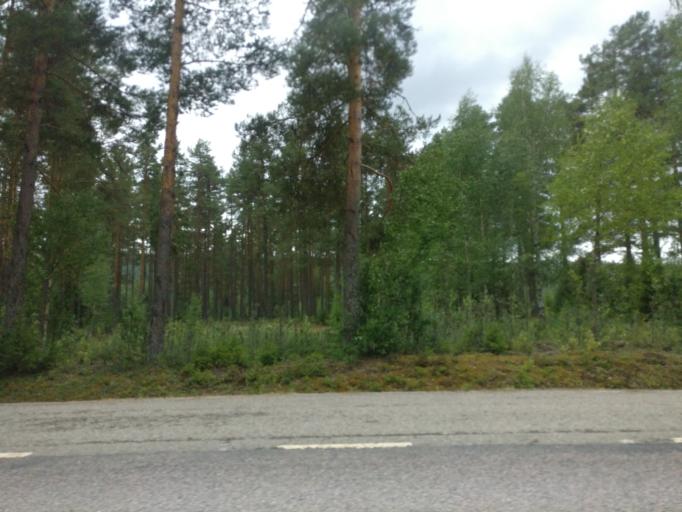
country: SE
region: Vaermland
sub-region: Torsby Kommun
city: Torsby
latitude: 60.7545
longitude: 12.7783
